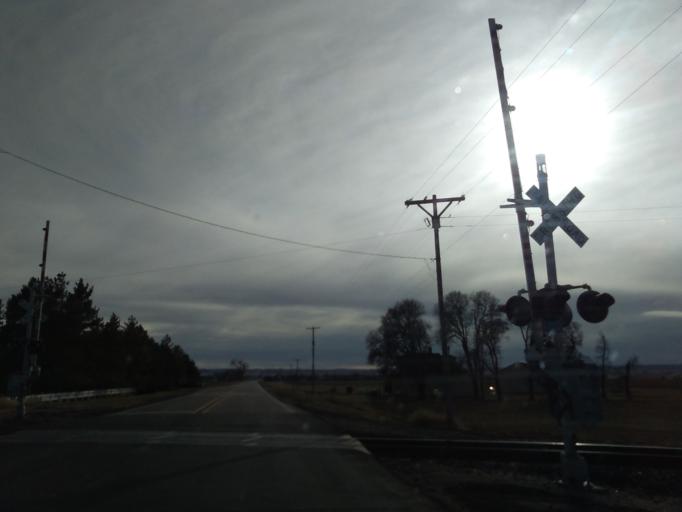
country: US
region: Nebraska
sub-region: Scotts Bluff County
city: Gering
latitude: 41.8128
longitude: -103.5194
